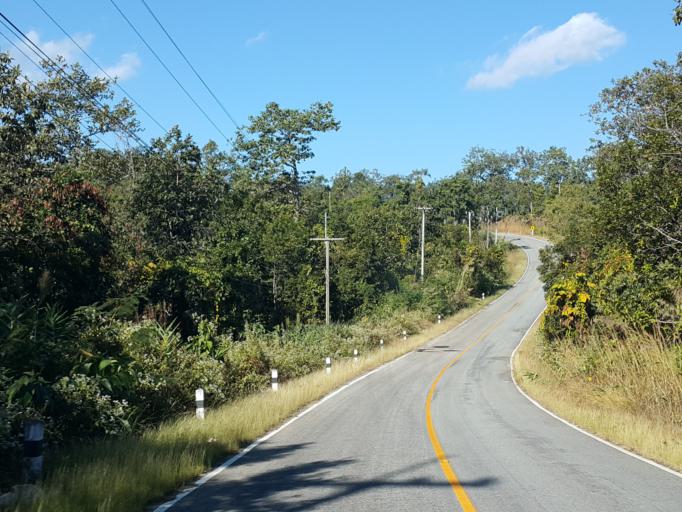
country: TH
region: Chiang Mai
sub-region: Amphoe Chiang Dao
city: Chiang Dao
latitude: 19.5269
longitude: 98.8928
